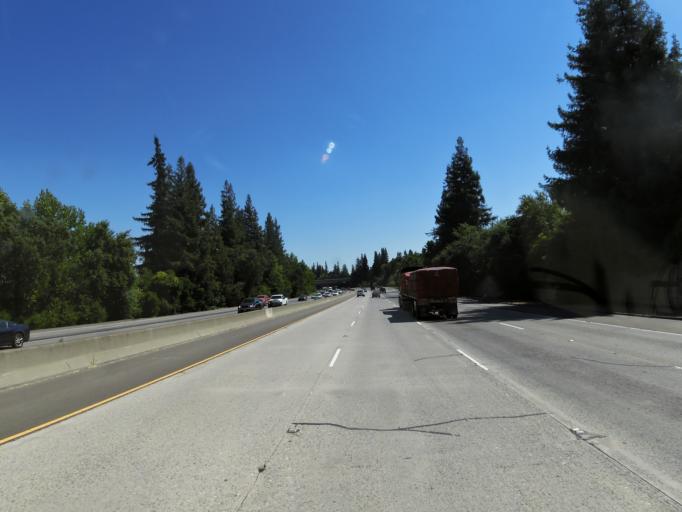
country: US
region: California
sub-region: Sacramento County
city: Parkway
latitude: 38.5140
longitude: -121.5223
